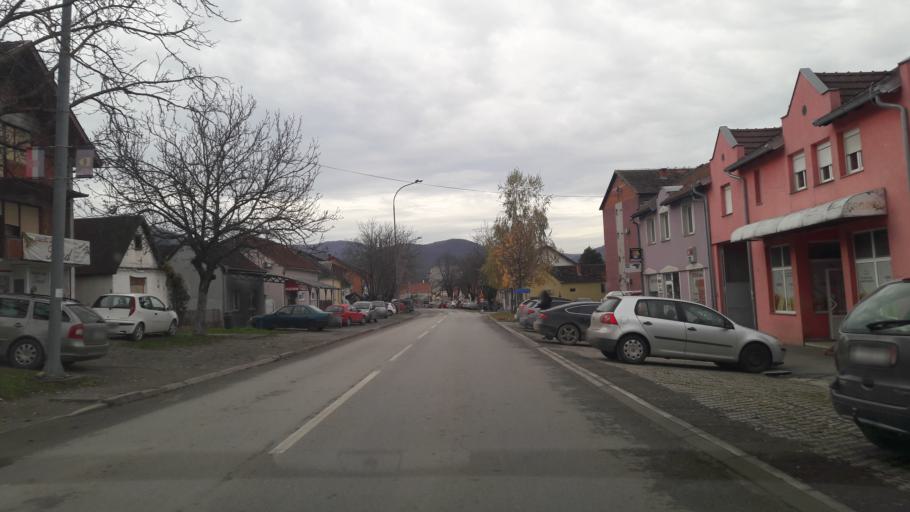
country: HR
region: Virovitick-Podravska
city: Orahovica
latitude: 45.5310
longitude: 17.8843
